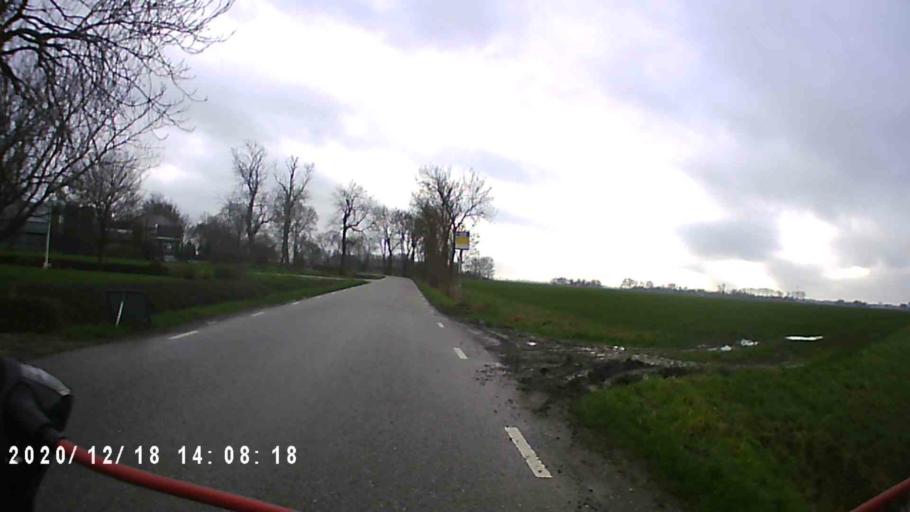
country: NL
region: Groningen
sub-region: Gemeente Bedum
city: Bedum
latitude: 53.2823
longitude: 6.6569
